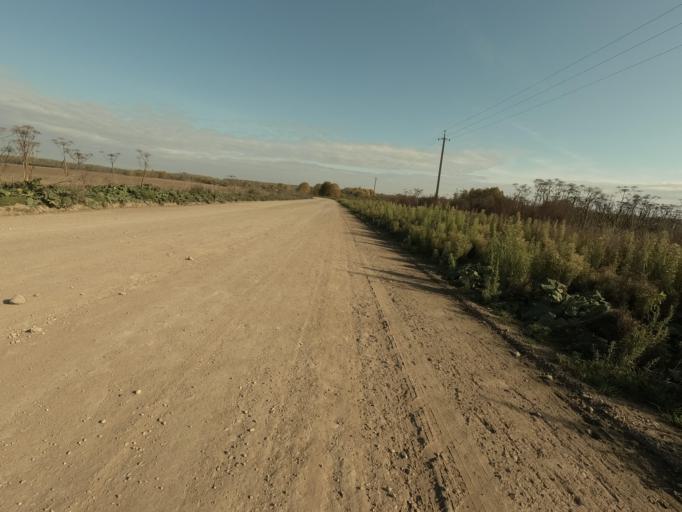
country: RU
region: Novgorod
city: Batetskiy
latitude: 58.8117
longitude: 30.6943
